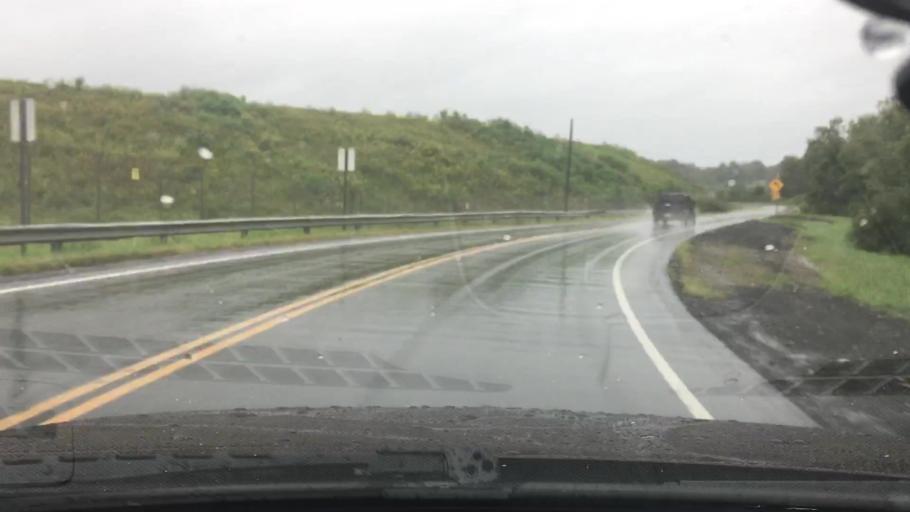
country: US
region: New York
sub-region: Dutchess County
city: Myers Corner
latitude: 41.6240
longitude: -73.8917
